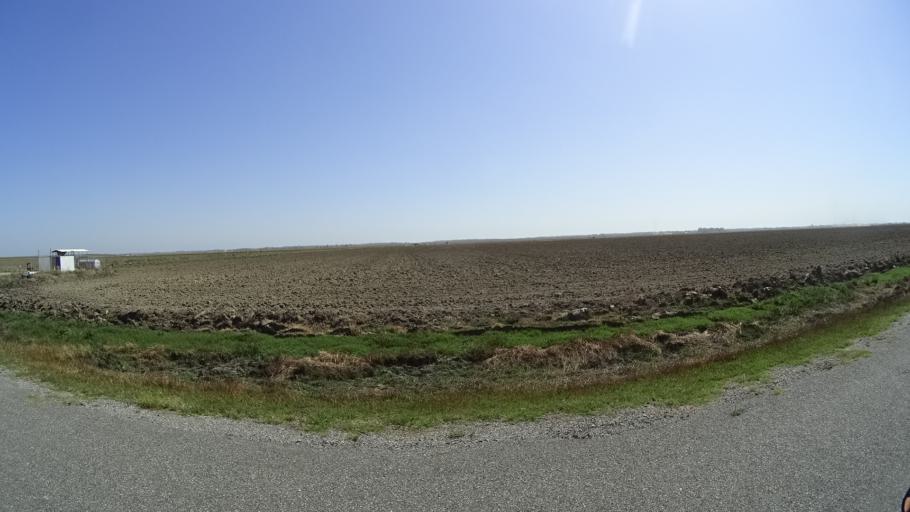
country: US
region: California
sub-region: Glenn County
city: Willows
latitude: 39.5068
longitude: -122.0653
